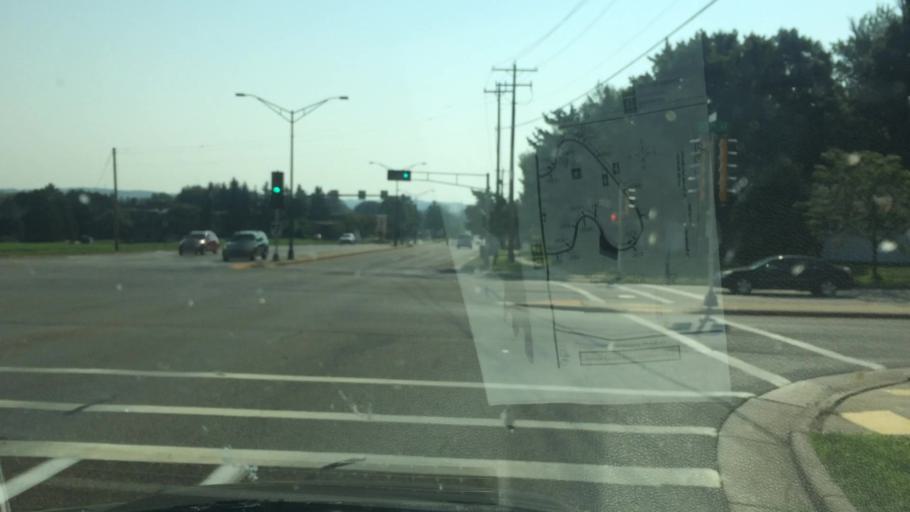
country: US
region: Wisconsin
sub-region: Marathon County
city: Wausau
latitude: 44.9699
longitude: -89.6527
